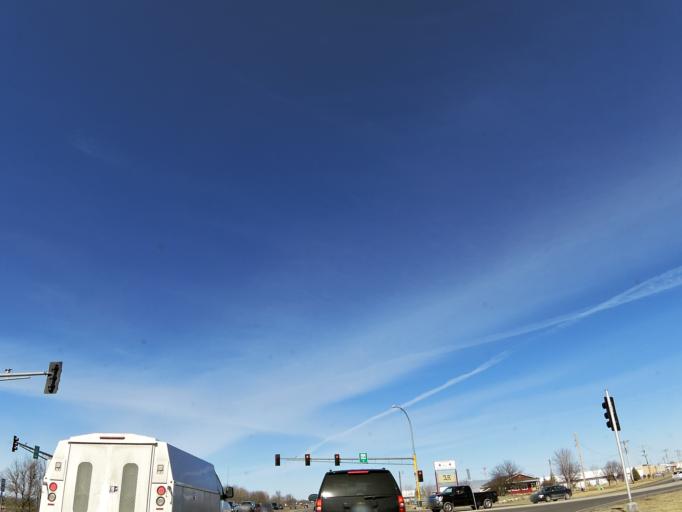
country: US
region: Minnesota
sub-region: Wright County
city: Buffalo
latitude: 45.1540
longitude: -93.8477
